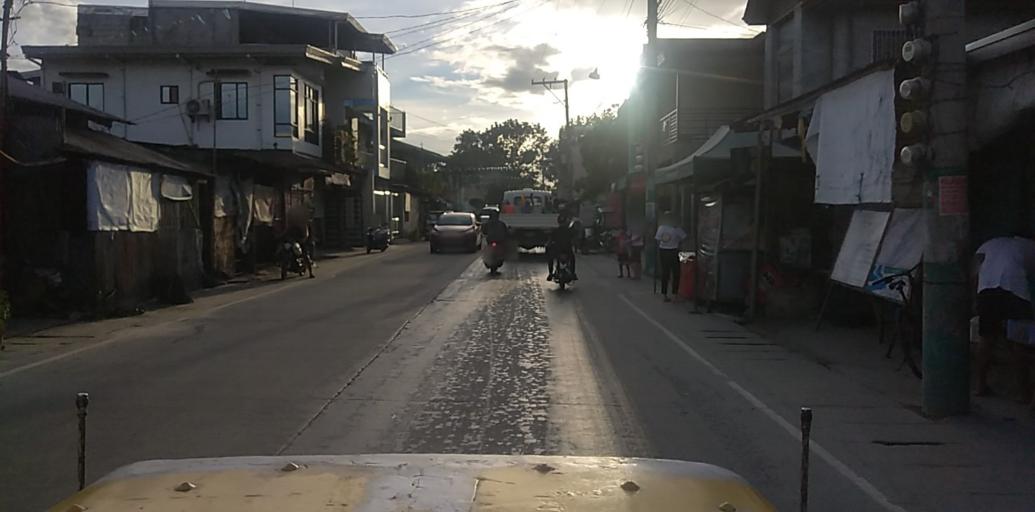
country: PH
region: Central Luzon
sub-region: Province of Pampanga
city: Malino
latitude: 15.1279
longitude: 120.6741
